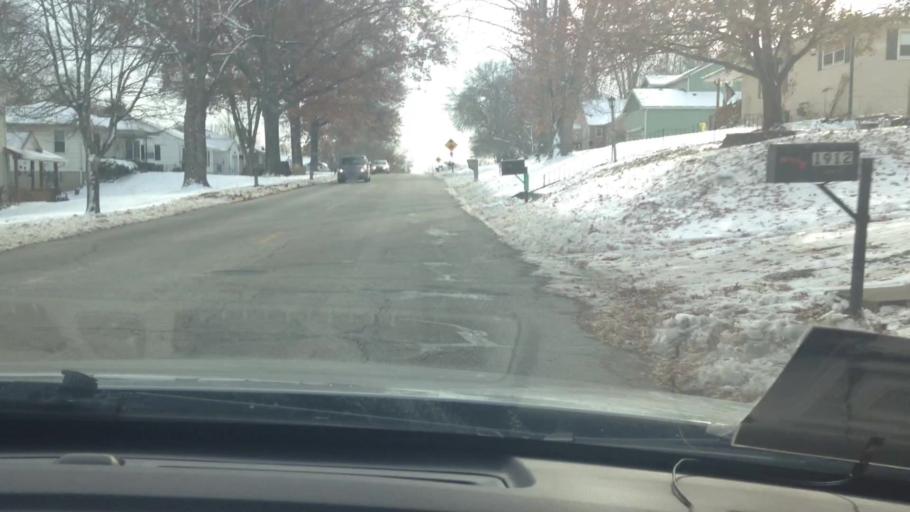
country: US
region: Kansas
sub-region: Leavenworth County
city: Leavenworth
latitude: 39.2979
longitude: -94.9210
